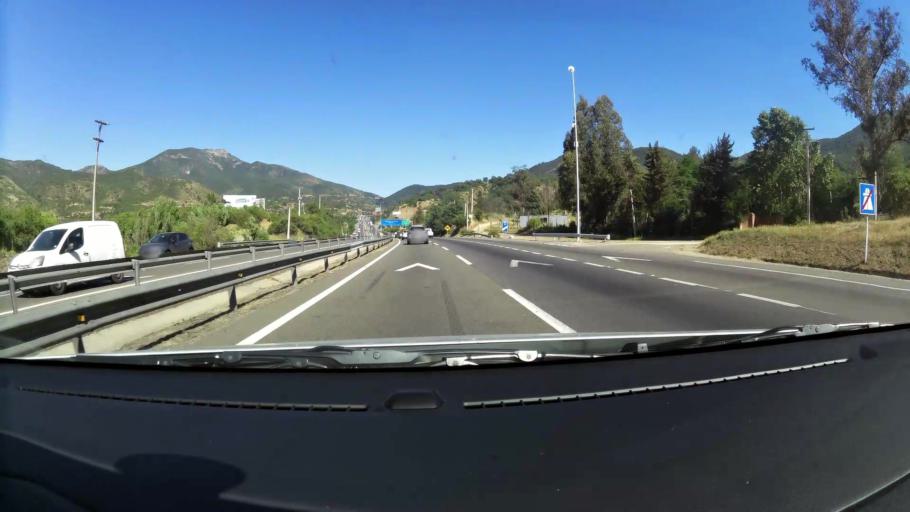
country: CL
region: Santiago Metropolitan
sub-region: Provincia de Melipilla
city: Melipilla
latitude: -33.3971
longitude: -71.2304
